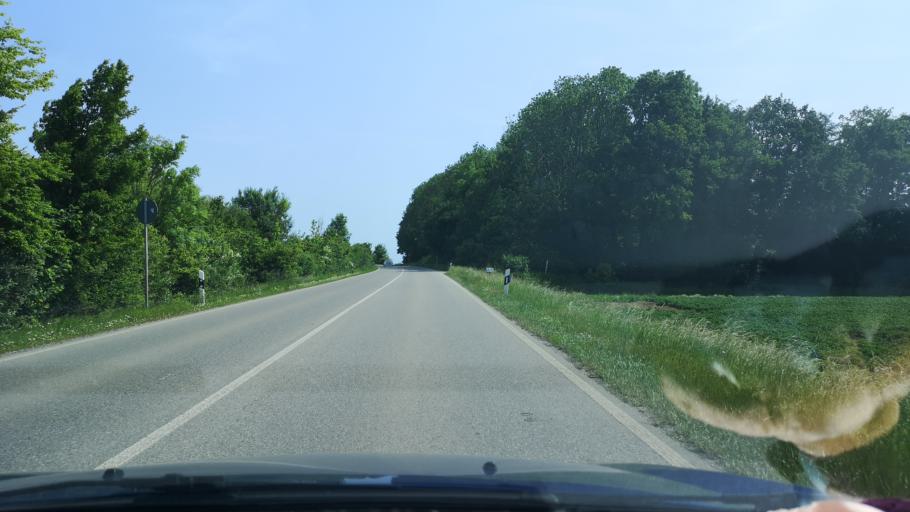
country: DE
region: Bavaria
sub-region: Upper Bavaria
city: Anzing
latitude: 48.1651
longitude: 11.8585
